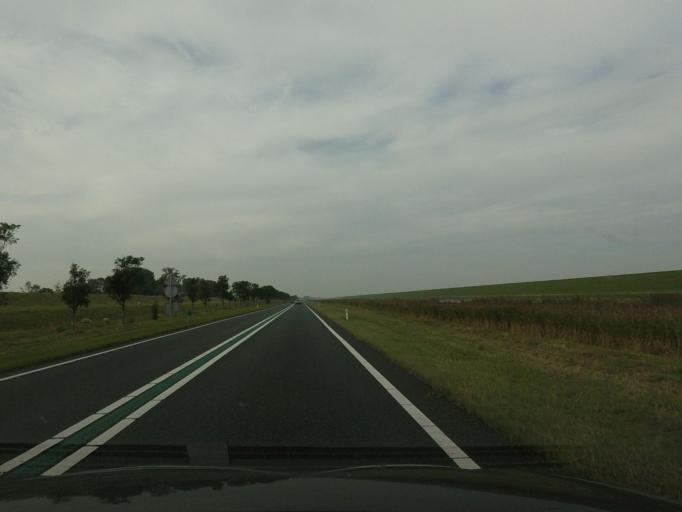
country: NL
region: North Holland
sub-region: Gemeente Den Helder
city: Den Helder
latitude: 52.8984
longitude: 4.8395
